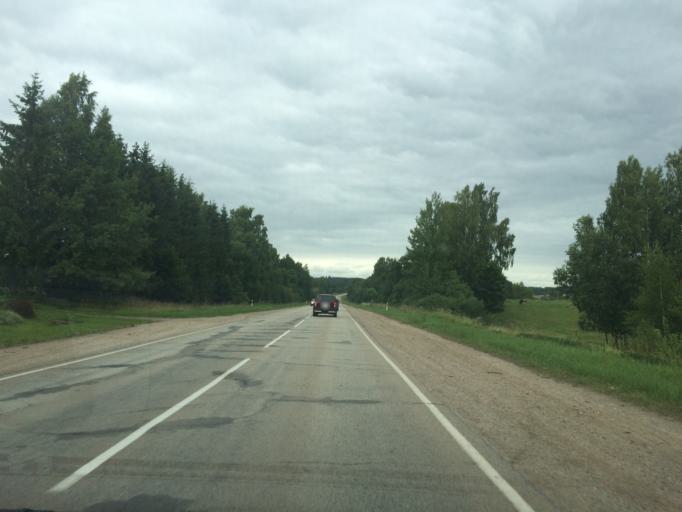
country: LV
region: Rezekne
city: Rezekne
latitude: 56.5608
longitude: 27.3640
